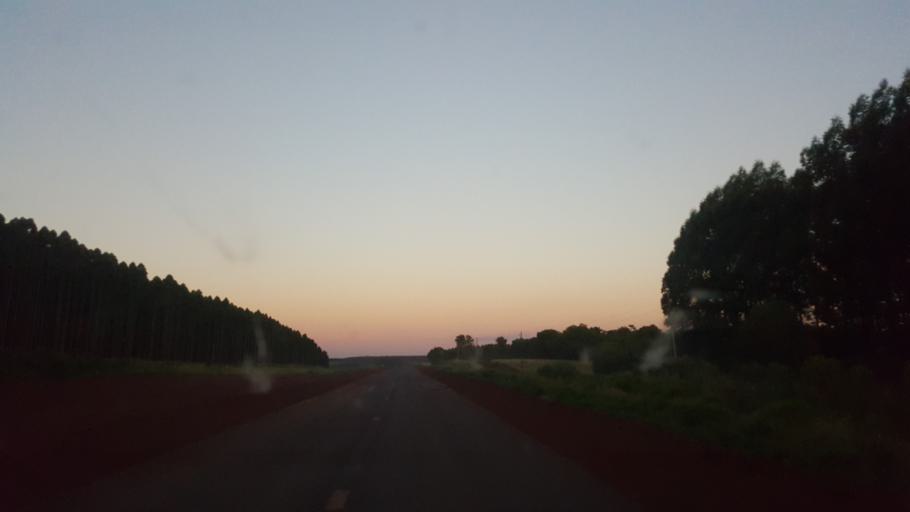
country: AR
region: Corrientes
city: Garruchos
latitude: -28.2431
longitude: -55.8336
